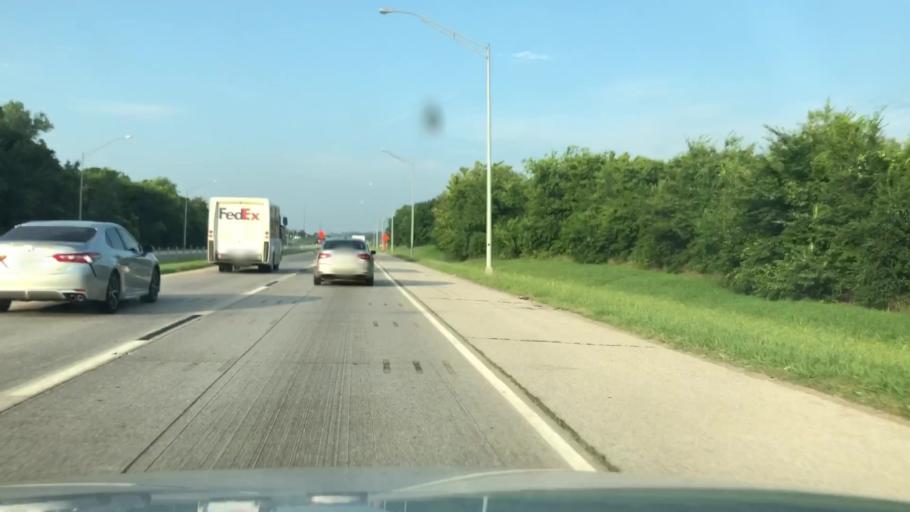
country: US
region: Oklahoma
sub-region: Tulsa County
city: Tulsa
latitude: 36.1818
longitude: -95.9663
